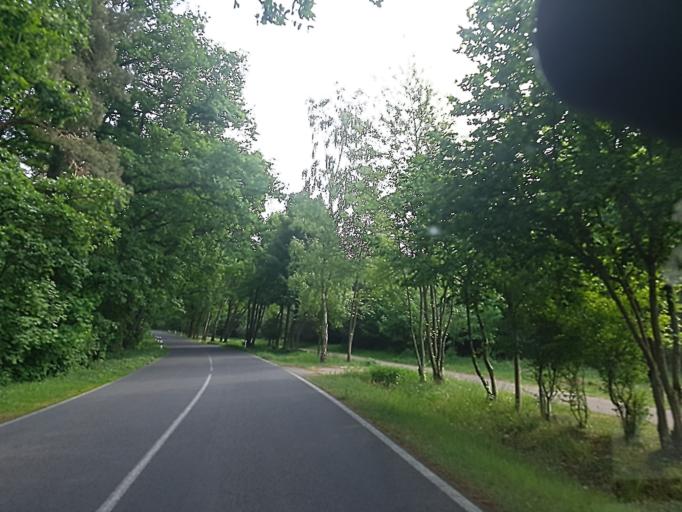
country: DE
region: Brandenburg
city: Belzig
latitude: 52.0364
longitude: 12.5768
